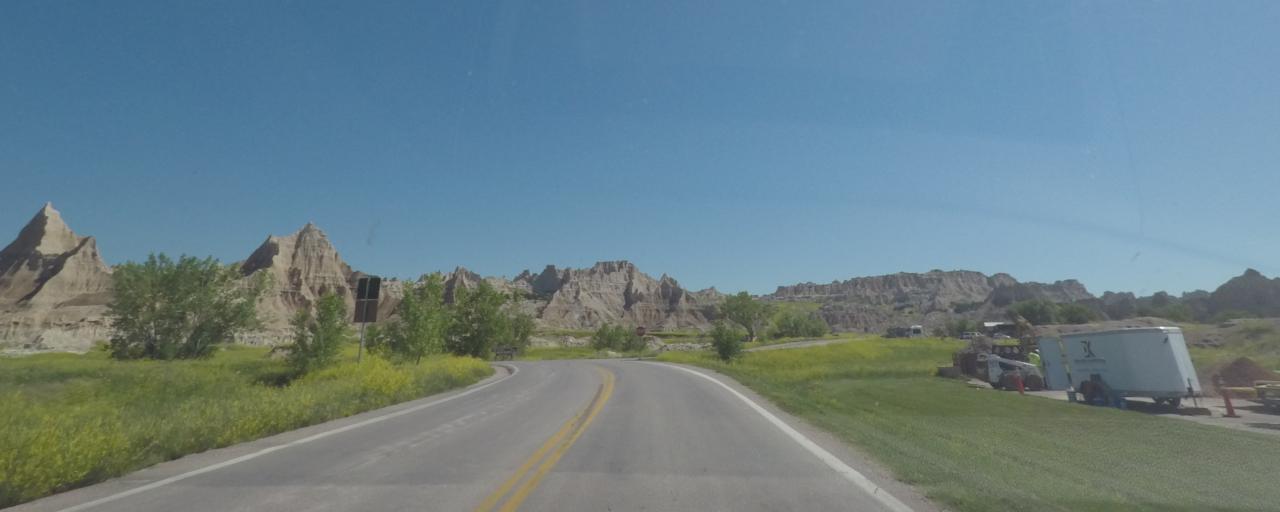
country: US
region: South Dakota
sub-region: Haakon County
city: Philip
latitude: 43.7470
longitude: -101.9480
